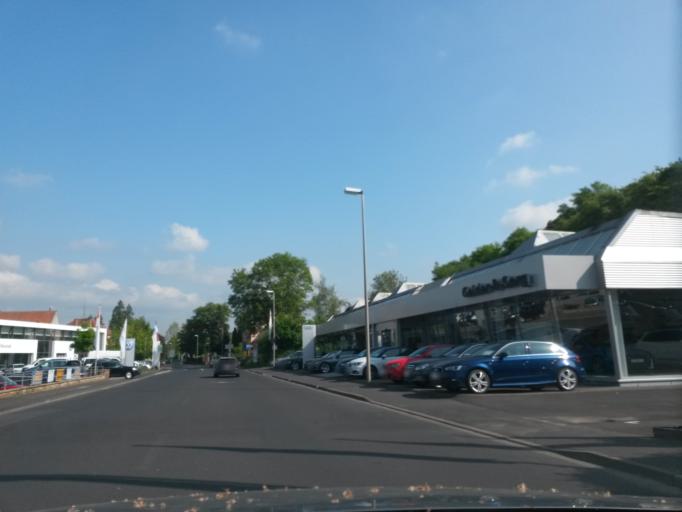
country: DE
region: Bavaria
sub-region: Regierungsbezirk Unterfranken
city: Bad Kissingen
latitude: 50.1853
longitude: 10.0778
